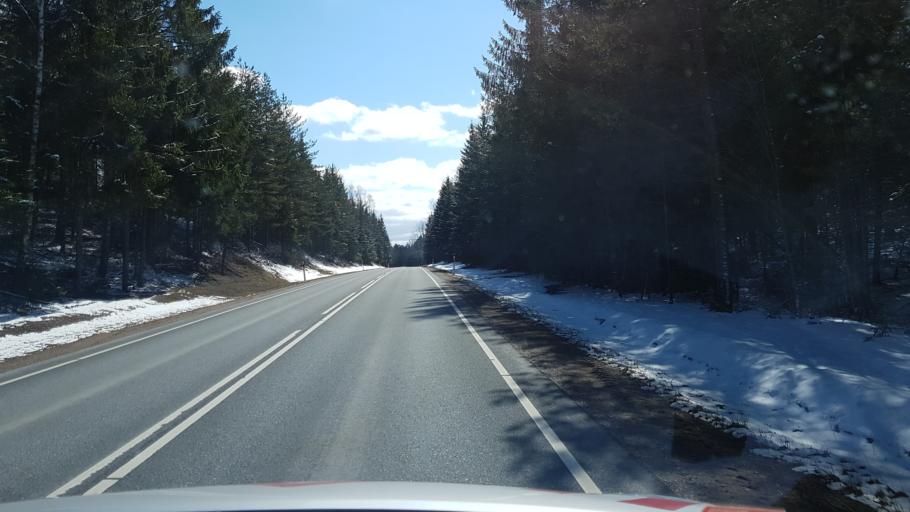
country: EE
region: Laeaene-Virumaa
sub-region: Tapa vald
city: Tapa
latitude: 59.4108
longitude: 26.0011
